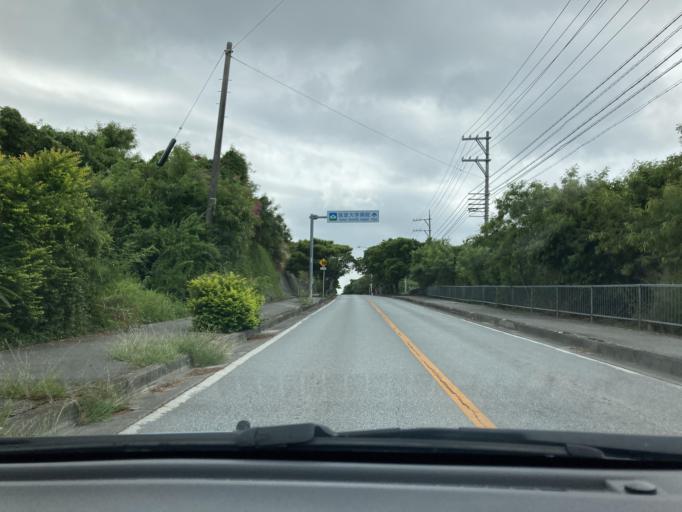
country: JP
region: Okinawa
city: Ginowan
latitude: 26.2675
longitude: 127.7766
